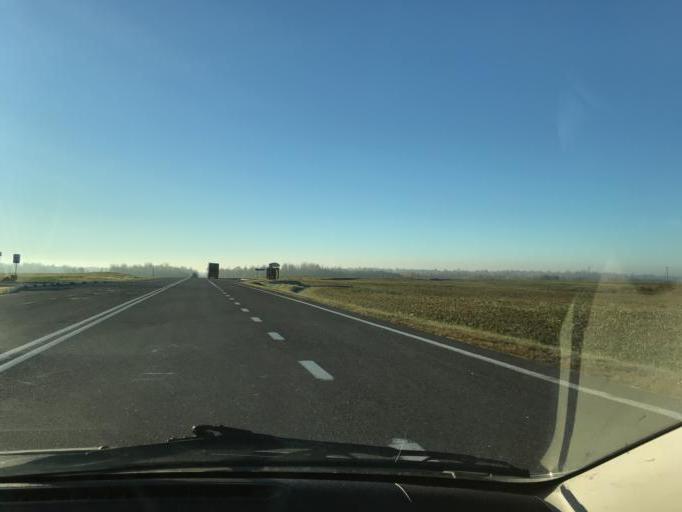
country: BY
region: Vitebsk
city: Vitebsk
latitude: 55.0003
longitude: 30.3368
